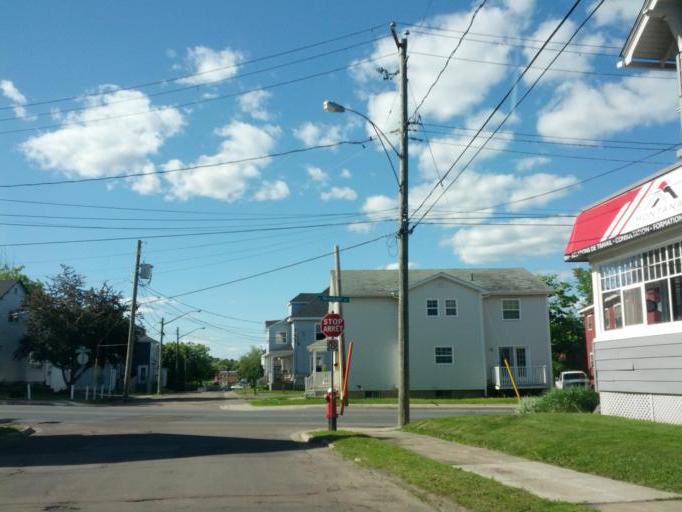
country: CA
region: New Brunswick
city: Moncton
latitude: 46.0942
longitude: -64.7769
